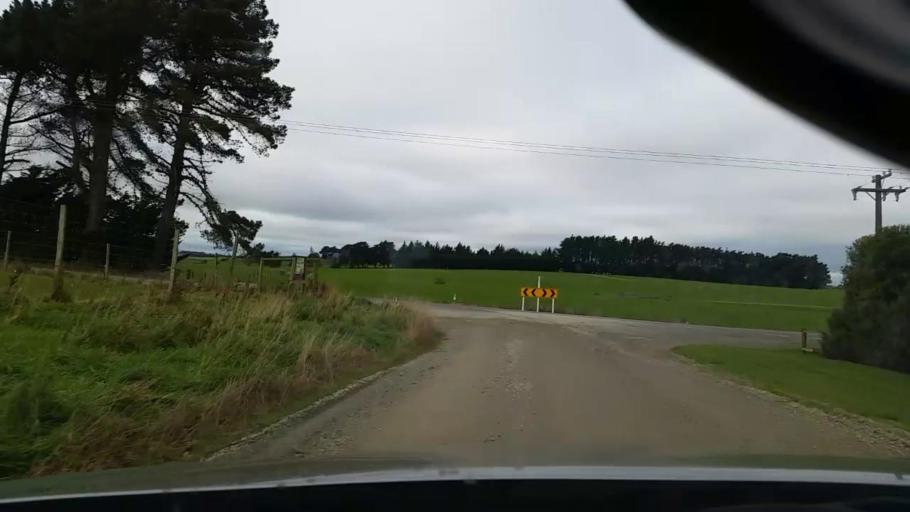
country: NZ
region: Southland
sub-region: Invercargill City
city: Invercargill
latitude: -46.3557
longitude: 168.4529
